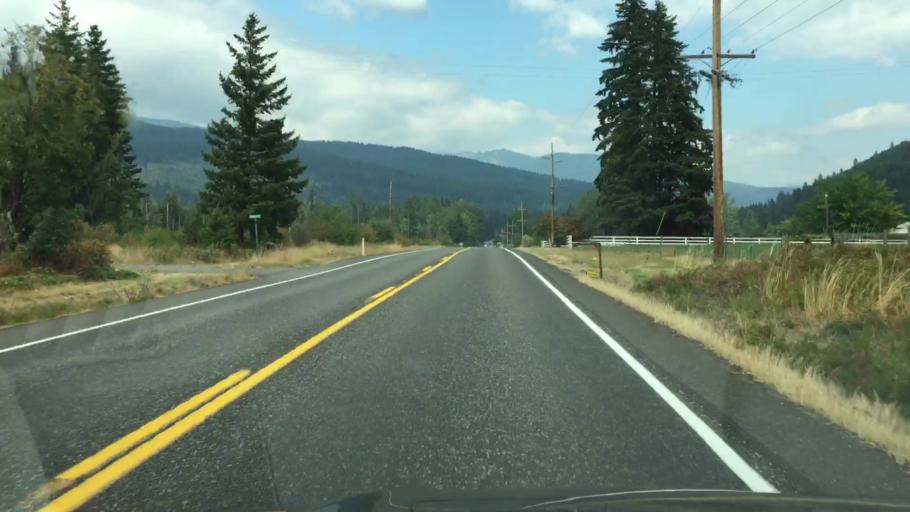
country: US
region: Washington
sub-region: Klickitat County
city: White Salmon
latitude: 45.8407
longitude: -121.5021
